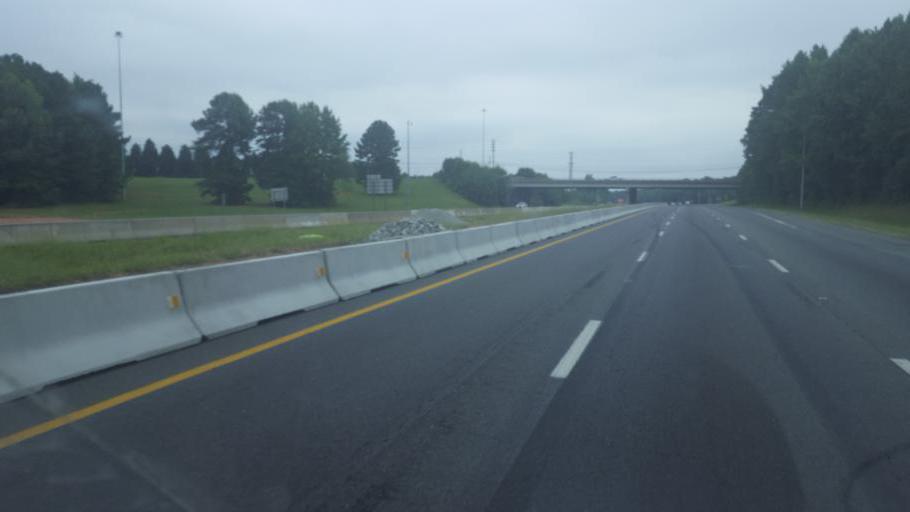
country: US
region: North Carolina
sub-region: Mecklenburg County
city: Charlotte
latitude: 35.3054
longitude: -80.8485
